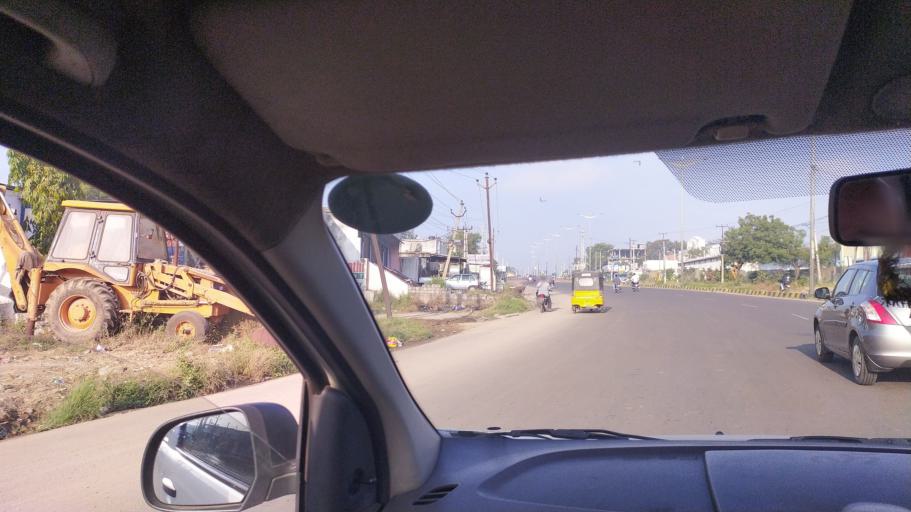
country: IN
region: Telangana
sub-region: Rangareddi
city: Balapur
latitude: 17.3150
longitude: 78.4582
